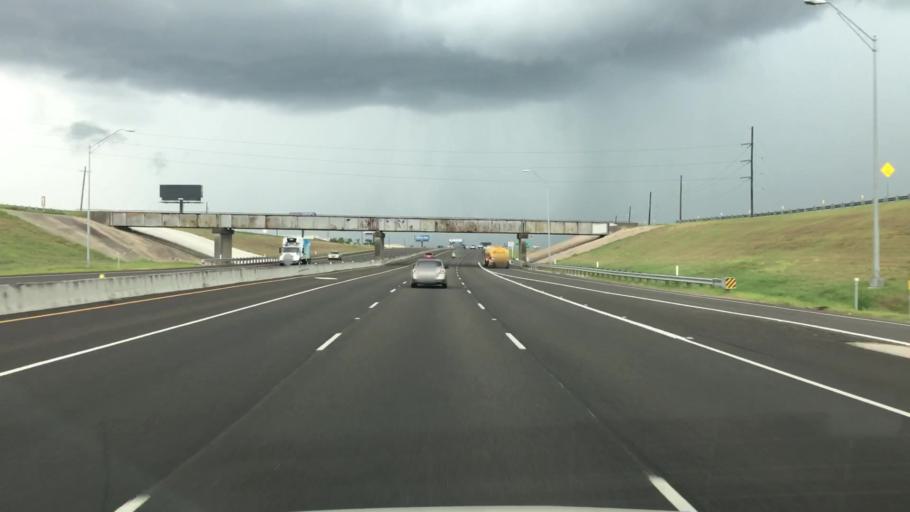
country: US
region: Texas
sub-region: Nueces County
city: Corpus Christi
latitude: 27.8057
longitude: -97.4878
